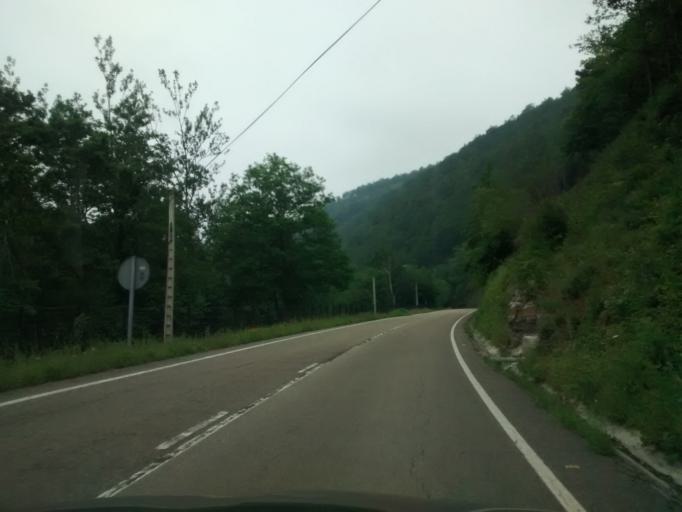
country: ES
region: Cantabria
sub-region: Provincia de Cantabria
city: Ruente
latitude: 43.1498
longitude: -4.2172
